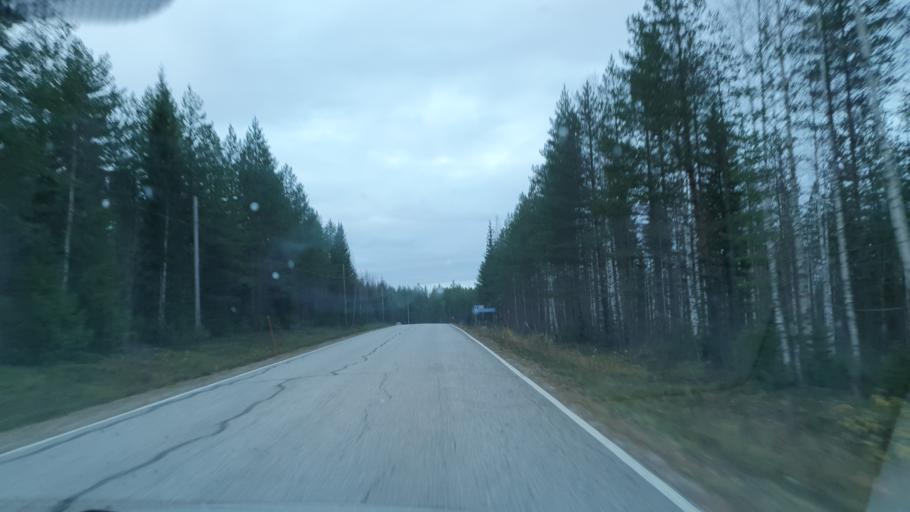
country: FI
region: Kainuu
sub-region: Kajaani
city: Ristijaervi
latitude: 64.4342
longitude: 28.3683
